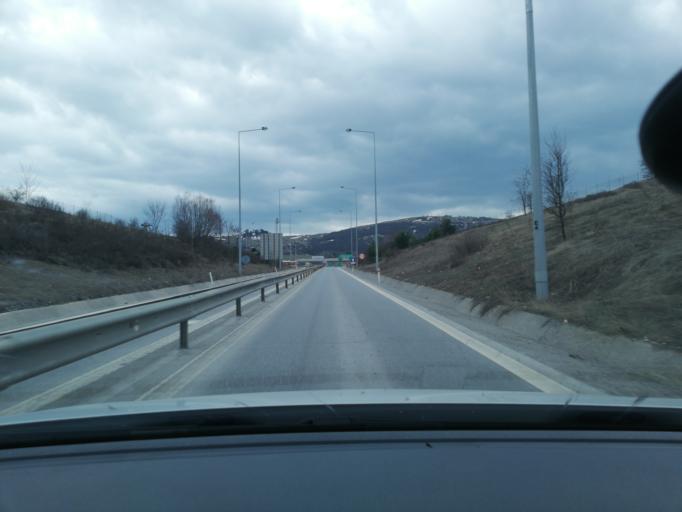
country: TR
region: Bolu
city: Yenicaga
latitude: 40.7710
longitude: 32.0080
